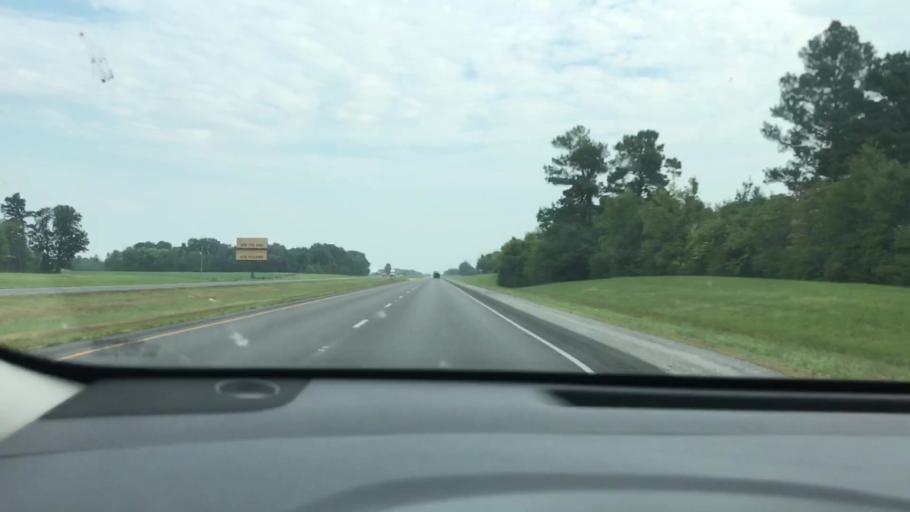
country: US
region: Kentucky
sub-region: Calloway County
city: Murray
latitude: 36.6804
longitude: -88.3026
